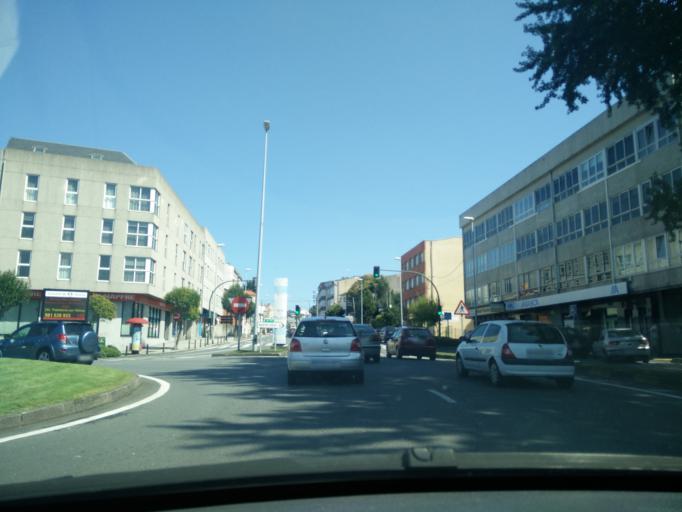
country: ES
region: Galicia
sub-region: Provincia da Coruna
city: A Coruna
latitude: 43.3344
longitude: -8.3781
